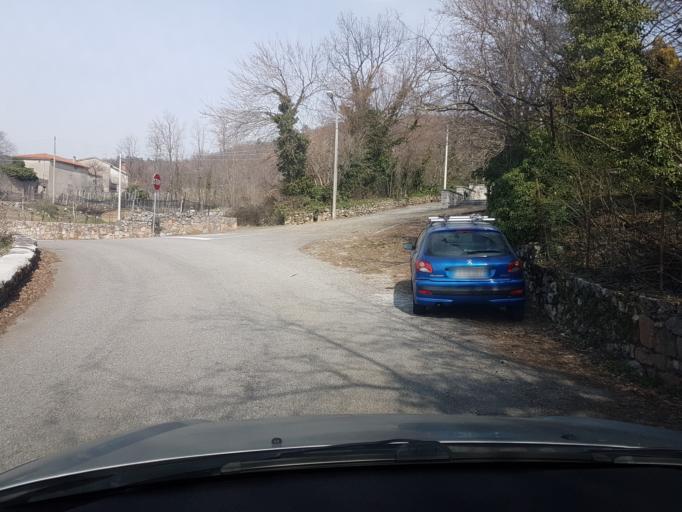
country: IT
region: Friuli Venezia Giulia
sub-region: Provincia di Trieste
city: Santa Croce
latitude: 45.7597
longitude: 13.7176
